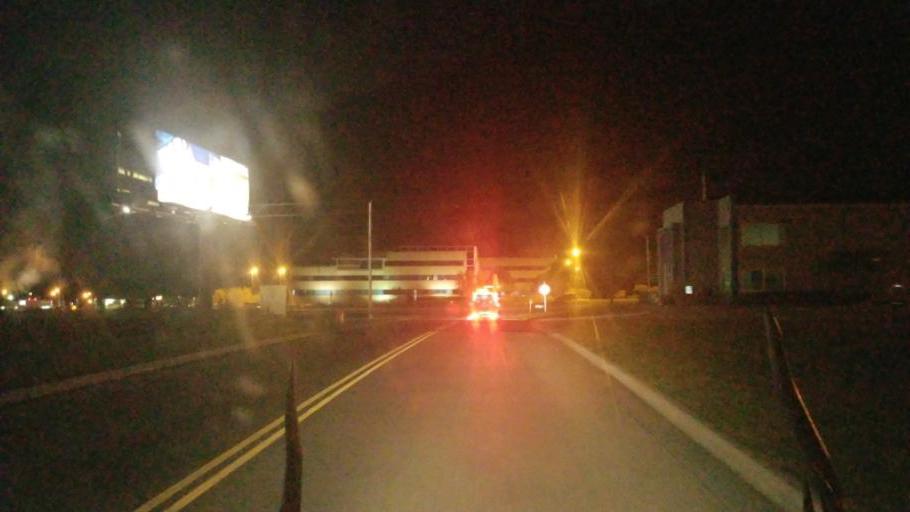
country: US
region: Missouri
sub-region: Jackson County
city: Grain Valley
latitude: 39.0229
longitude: -94.2008
